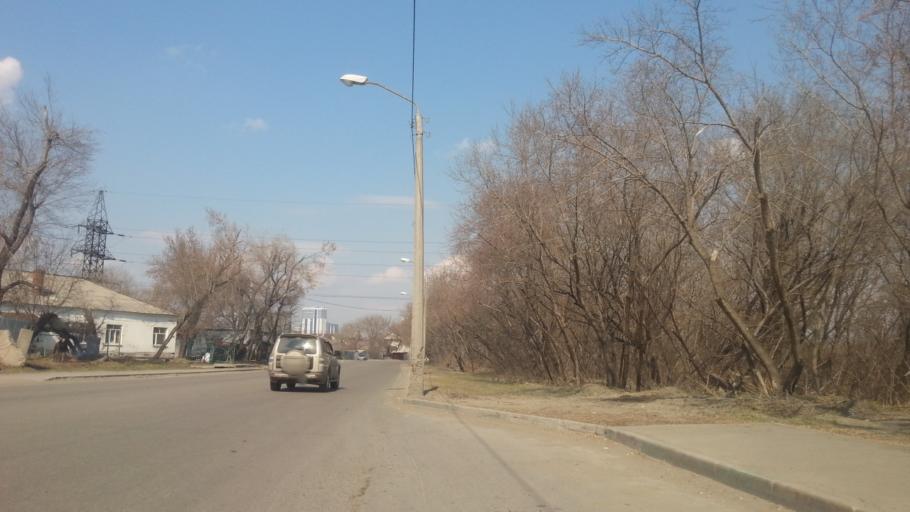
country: RU
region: Altai Krai
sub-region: Gorod Barnaulskiy
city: Barnaul
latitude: 53.3206
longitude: 83.7633
